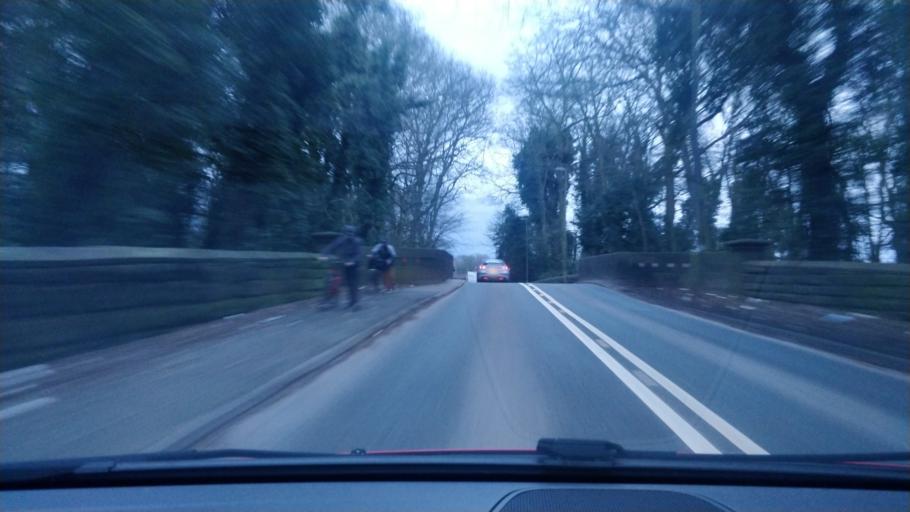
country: GB
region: England
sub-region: Knowsley
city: Kirkby
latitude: 53.4415
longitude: -2.8958
